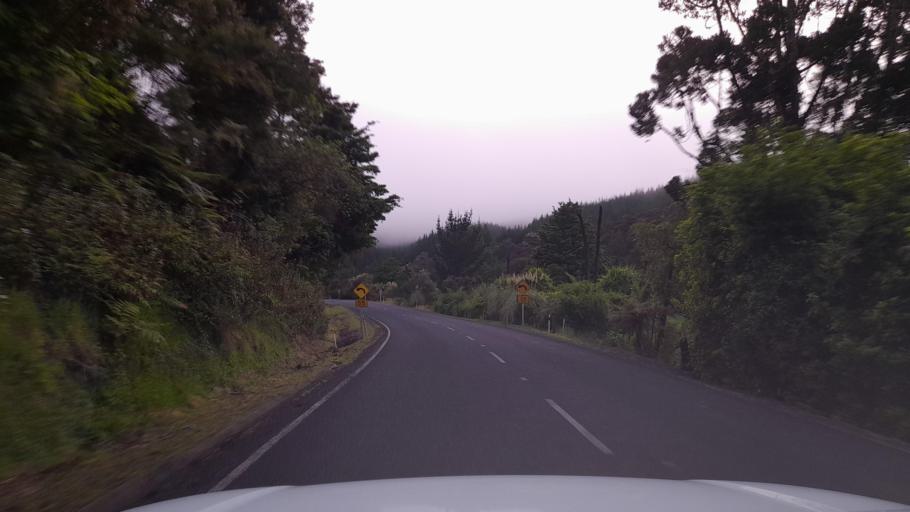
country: NZ
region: Northland
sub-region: Kaipara District
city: Dargaville
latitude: -35.6346
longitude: 173.8545
